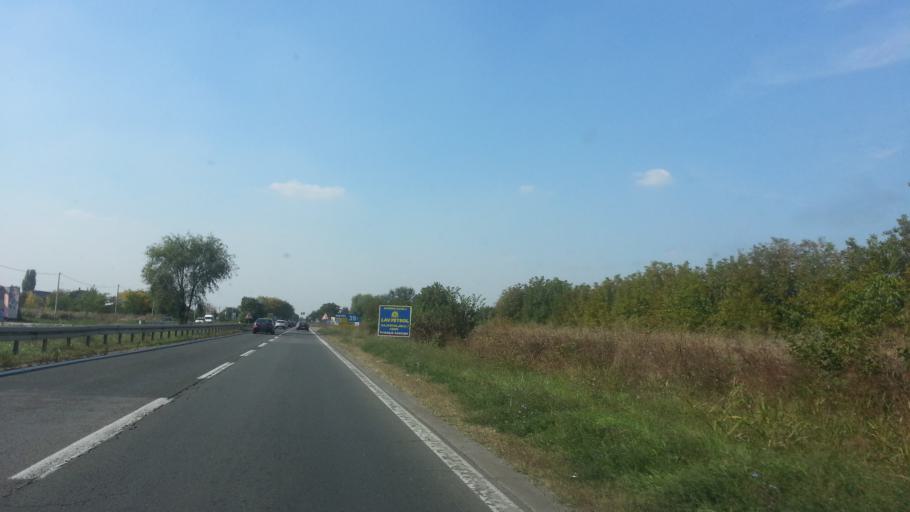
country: RS
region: Central Serbia
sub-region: Belgrade
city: Zemun
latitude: 44.8594
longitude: 20.3569
